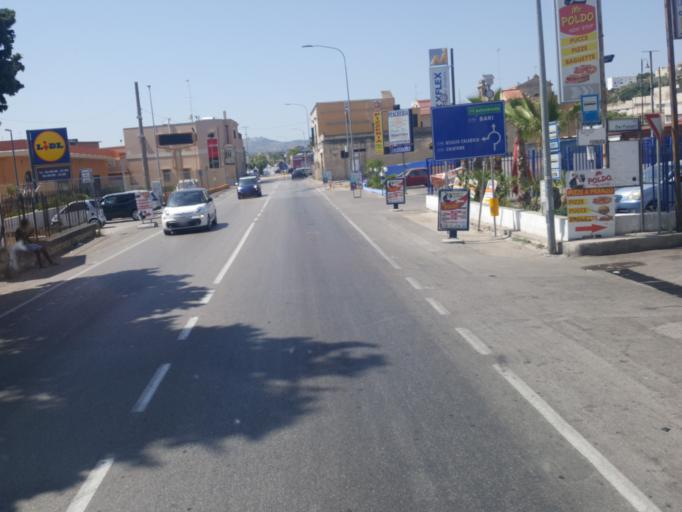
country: IT
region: Apulia
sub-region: Provincia di Taranto
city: Massafra
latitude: 40.5849
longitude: 17.1092
